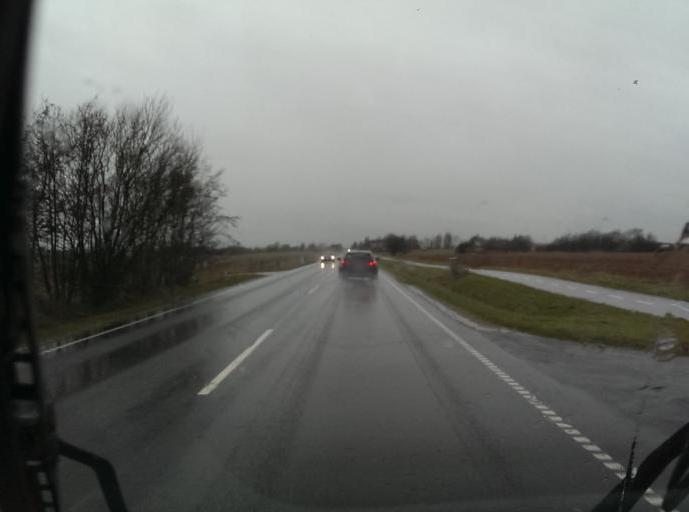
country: DK
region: South Denmark
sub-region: Varde Kommune
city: Olgod
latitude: 55.7416
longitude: 8.6185
